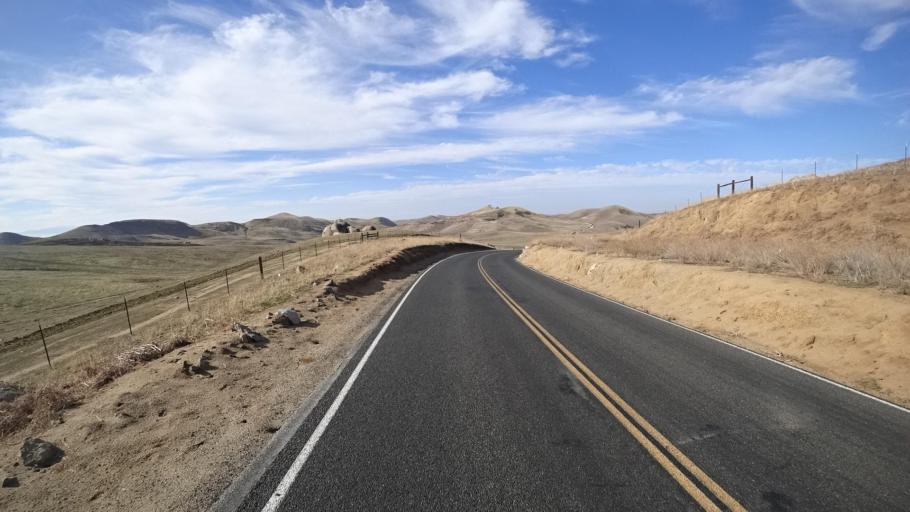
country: US
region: California
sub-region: Kern County
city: Oildale
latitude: 35.6122
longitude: -118.8651
